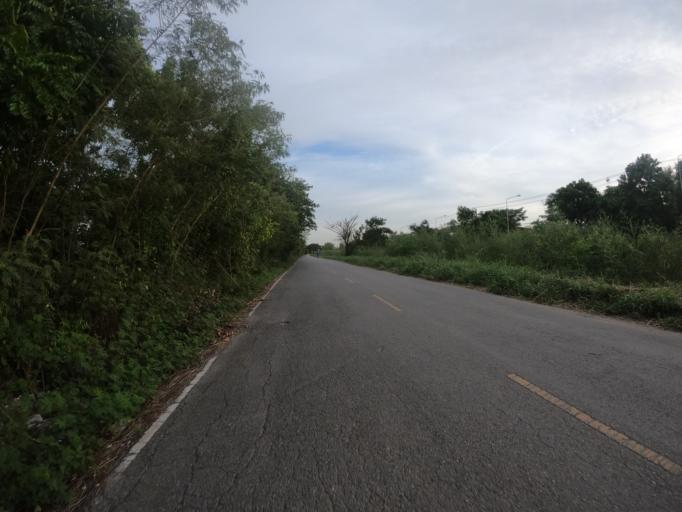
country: TH
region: Pathum Thani
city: Ban Rangsit
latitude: 14.0320
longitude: 100.8009
